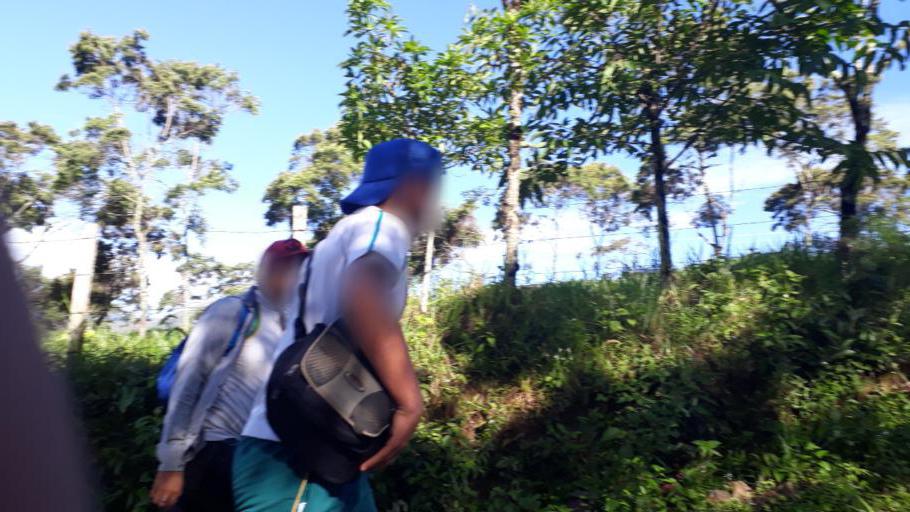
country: CO
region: Casanare
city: Nunchia
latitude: 5.6483
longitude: -72.4246
